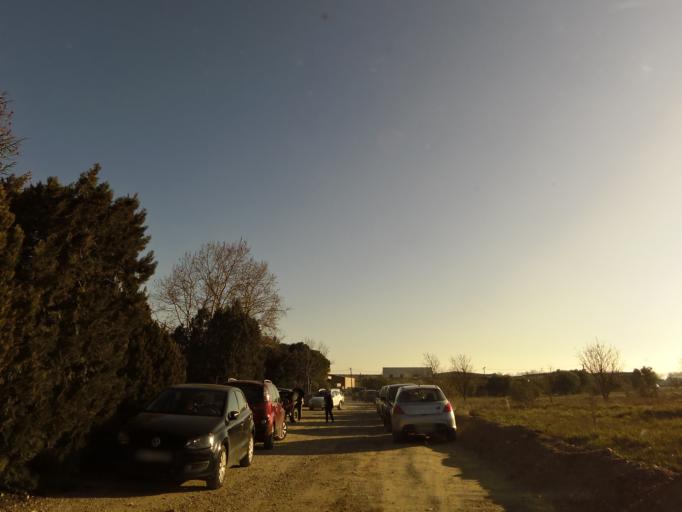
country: FR
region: Languedoc-Roussillon
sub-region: Departement du Gard
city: Codognan
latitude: 43.7294
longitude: 4.2136
